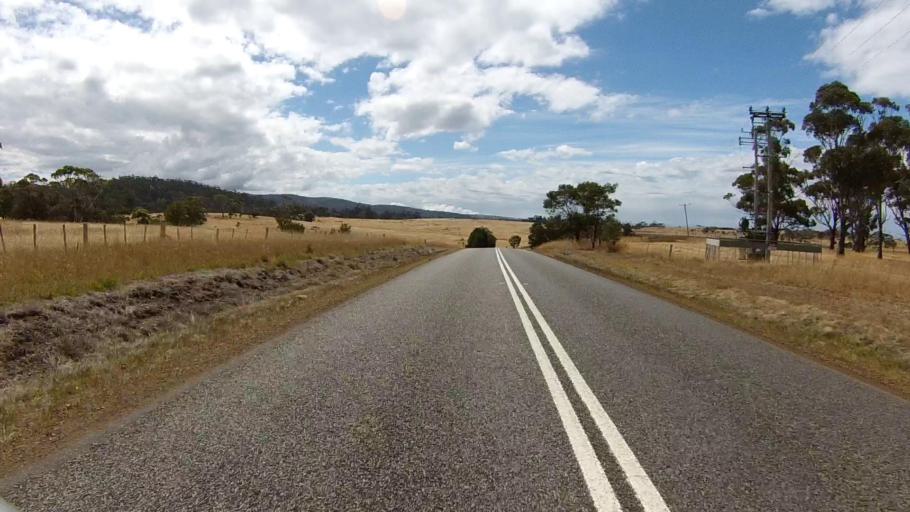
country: AU
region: Tasmania
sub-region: Sorell
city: Sorell
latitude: -42.2830
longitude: 147.9984
